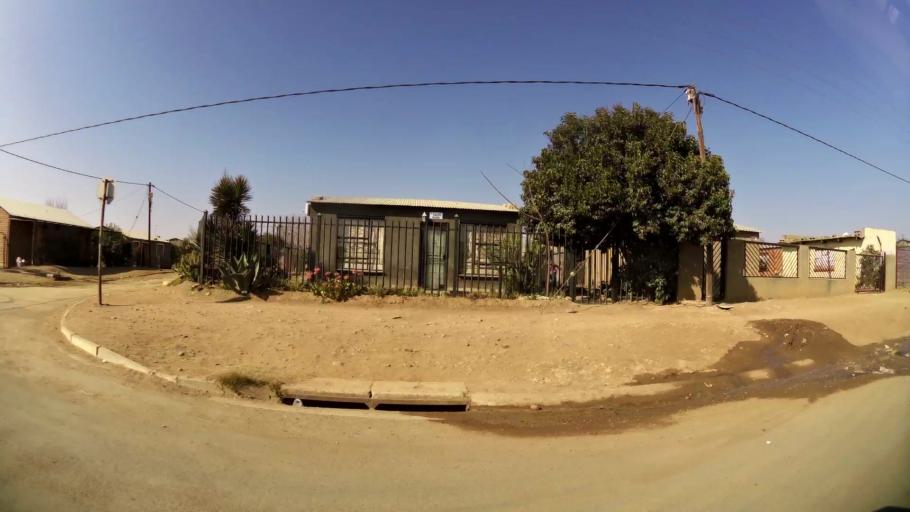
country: ZA
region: Orange Free State
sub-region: Mangaung Metropolitan Municipality
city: Bloemfontein
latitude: -29.1979
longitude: 26.2575
